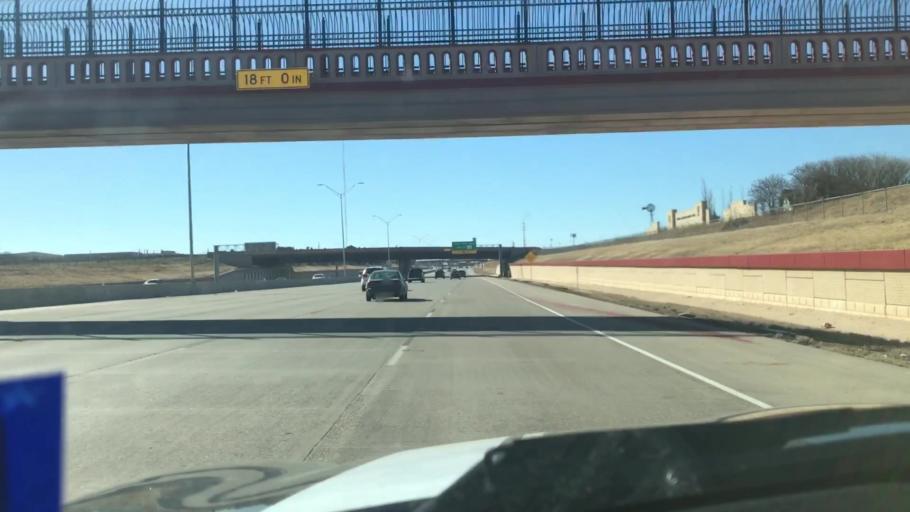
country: US
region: Texas
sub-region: Lubbock County
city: Lubbock
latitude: 33.5891
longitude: -101.8821
